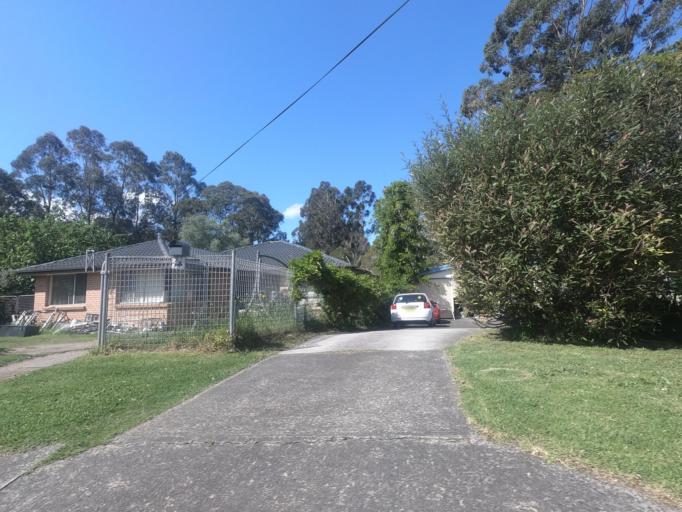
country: AU
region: New South Wales
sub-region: Wollongong
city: Cordeaux Heights
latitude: -34.4556
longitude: 150.8359
